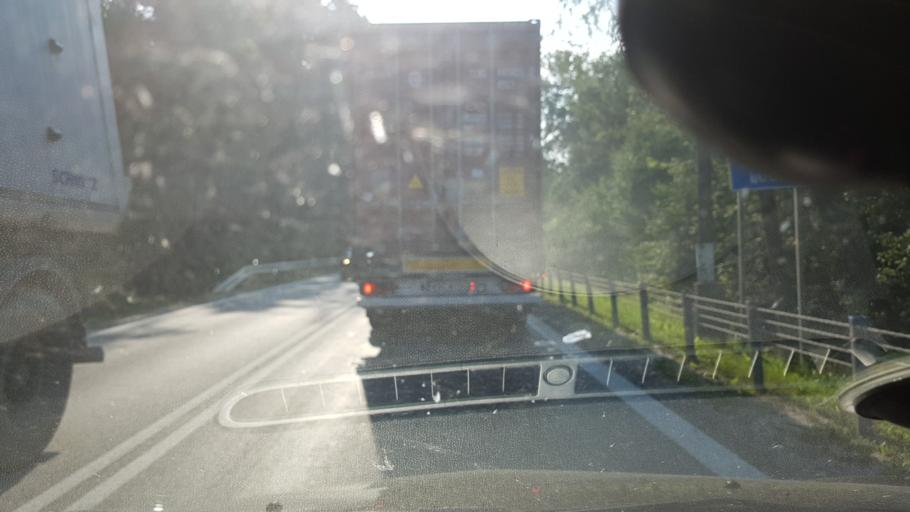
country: PL
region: Lesser Poland Voivodeship
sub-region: Powiat suski
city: Naprawa
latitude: 49.6539
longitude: 19.9038
